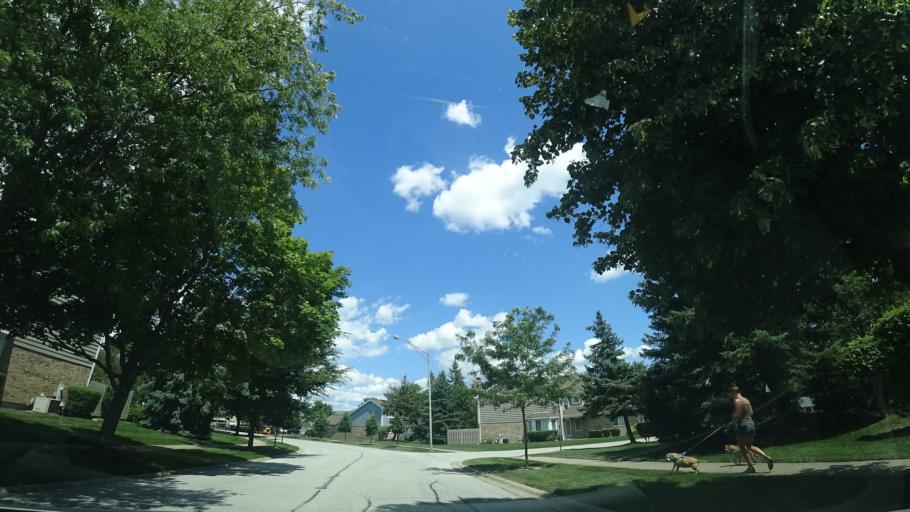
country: US
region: Illinois
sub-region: Will County
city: Mokena
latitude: 41.5759
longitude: -87.8936
